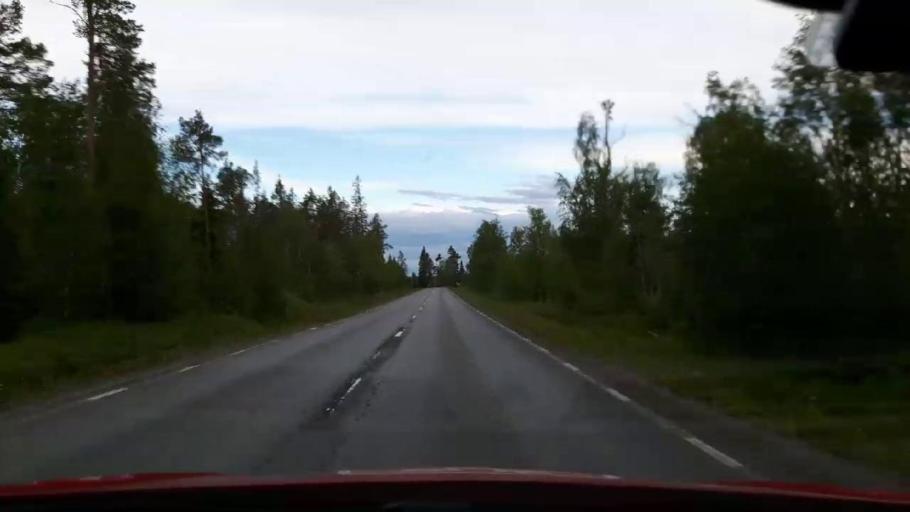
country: SE
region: Jaemtland
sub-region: Bergs Kommun
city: Hoverberg
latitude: 63.0010
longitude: 14.4848
